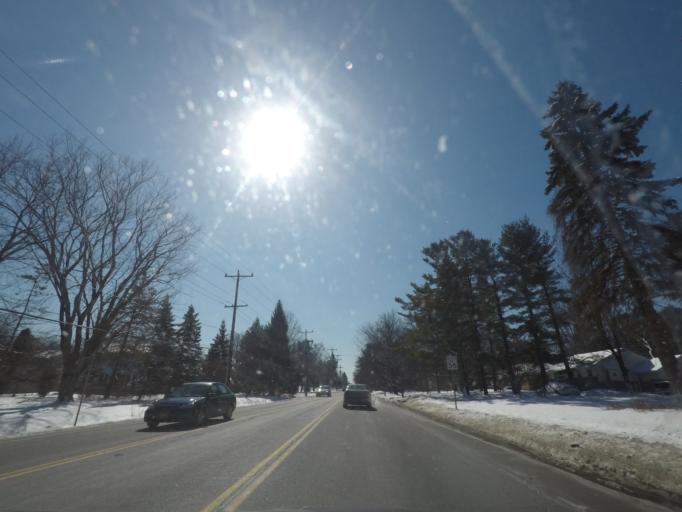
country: US
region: New York
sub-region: Schenectady County
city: Schenectady
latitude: 42.8270
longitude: -73.8921
